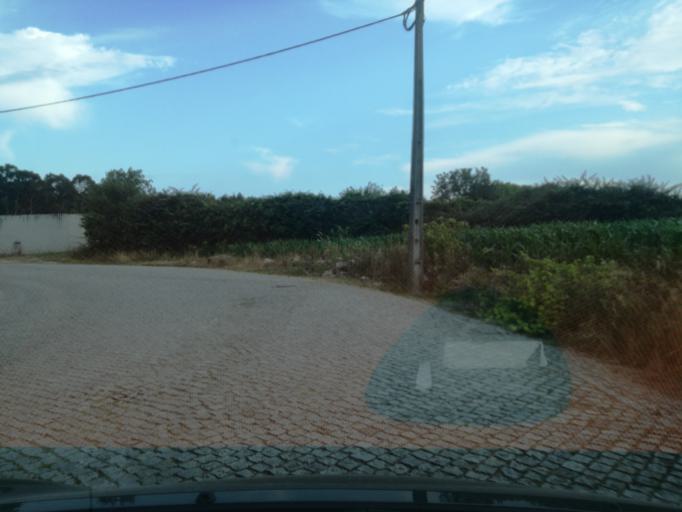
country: PT
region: Porto
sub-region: Maia
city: Anta
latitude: 41.2557
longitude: -8.6139
